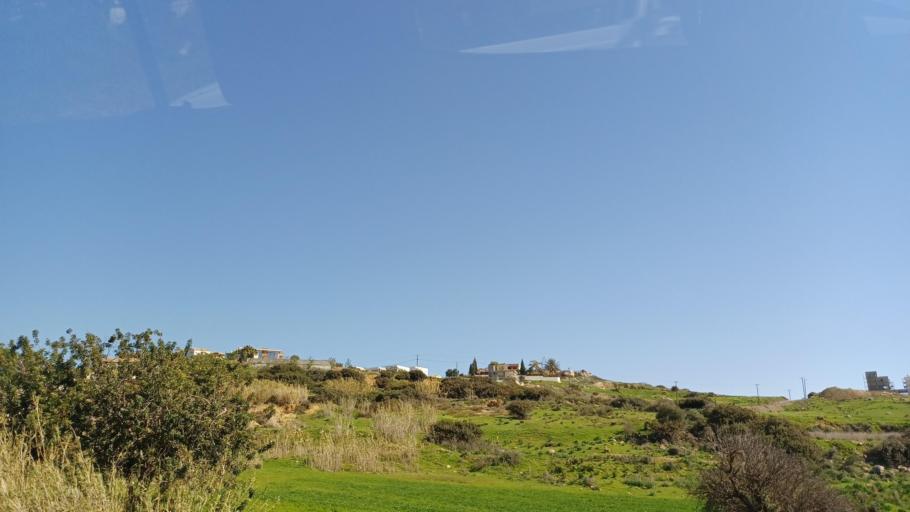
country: CY
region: Limassol
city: Parekklisha
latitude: 34.7359
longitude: 33.1527
